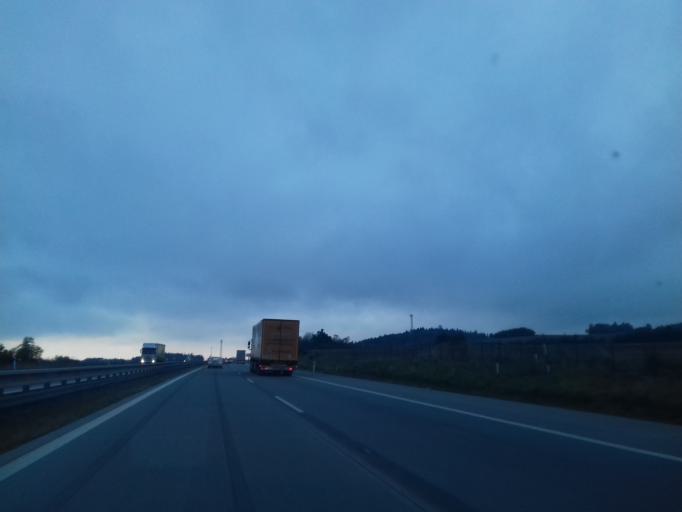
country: CZ
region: Vysocina
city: Krizanov
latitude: 49.3056
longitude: 16.1281
